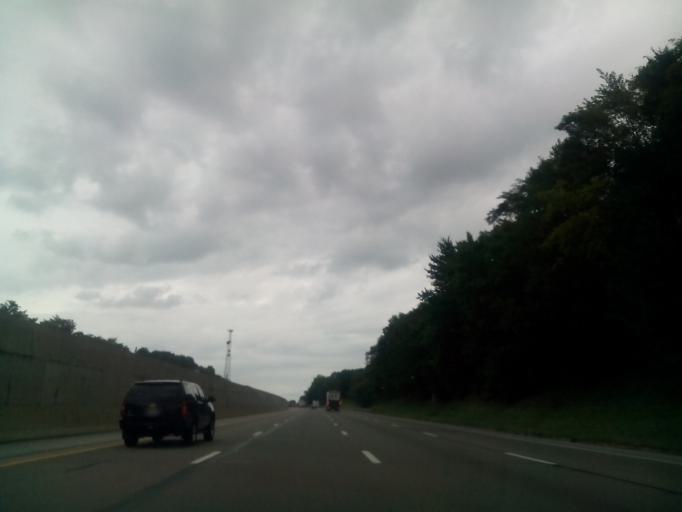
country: US
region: Ohio
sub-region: Erie County
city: Huron
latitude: 41.3288
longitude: -82.4864
